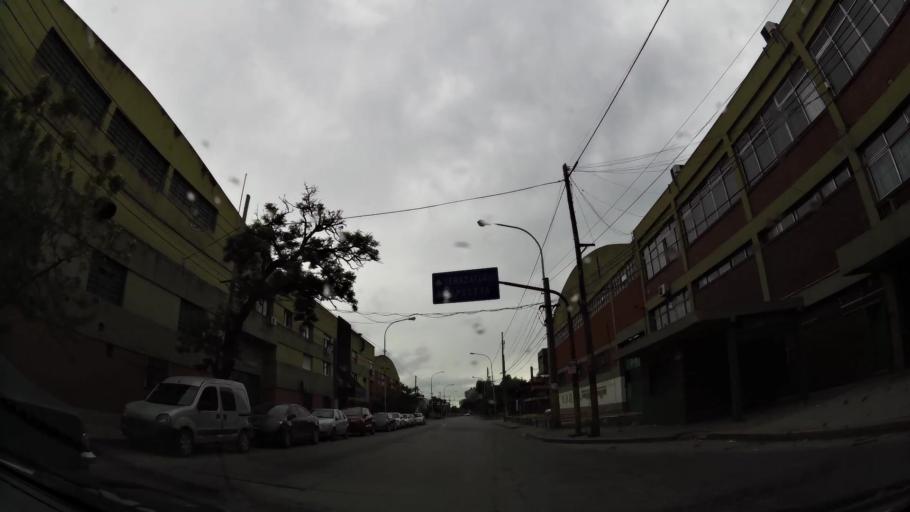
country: AR
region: Buenos Aires
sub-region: Partido de Quilmes
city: Quilmes
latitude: -34.7850
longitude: -58.2529
